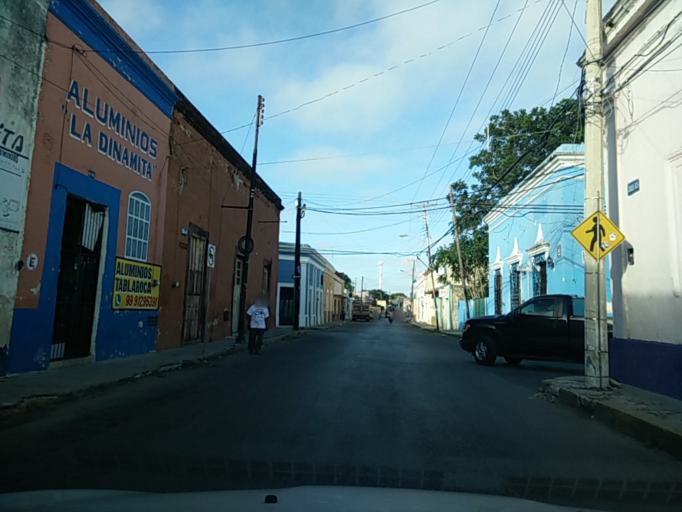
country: MX
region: Yucatan
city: Merida
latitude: 20.9668
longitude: -89.6380
